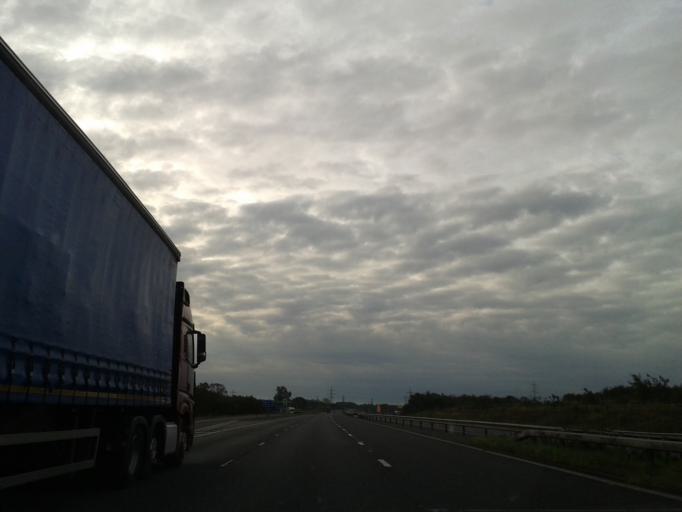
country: GB
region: England
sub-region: Cumbria
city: Carlisle
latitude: 54.9545
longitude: -2.9833
